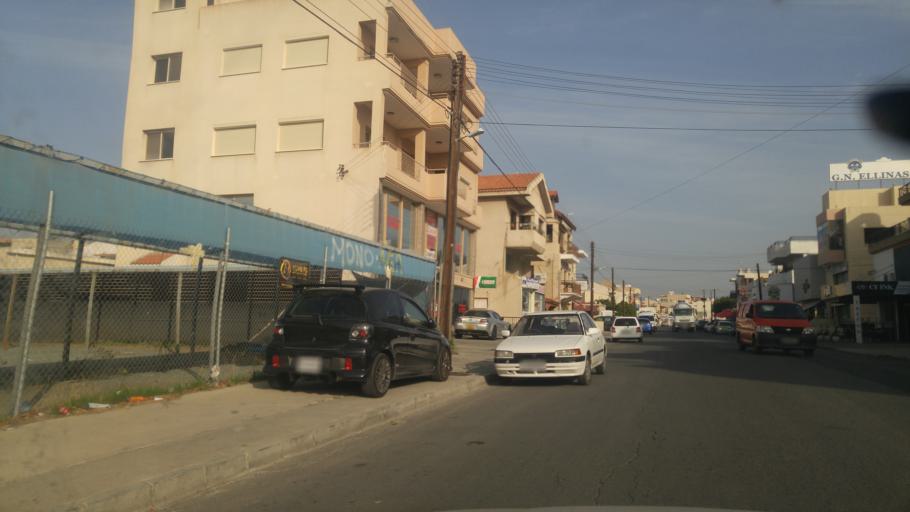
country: CY
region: Limassol
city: Limassol
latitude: 34.6655
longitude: 33.0039
